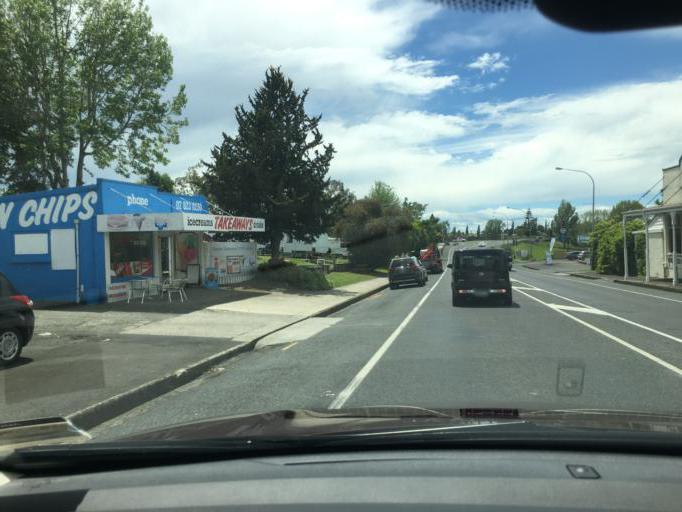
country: NZ
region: Waikato
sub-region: Hamilton City
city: Hamilton
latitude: -37.9186
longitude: 175.3068
